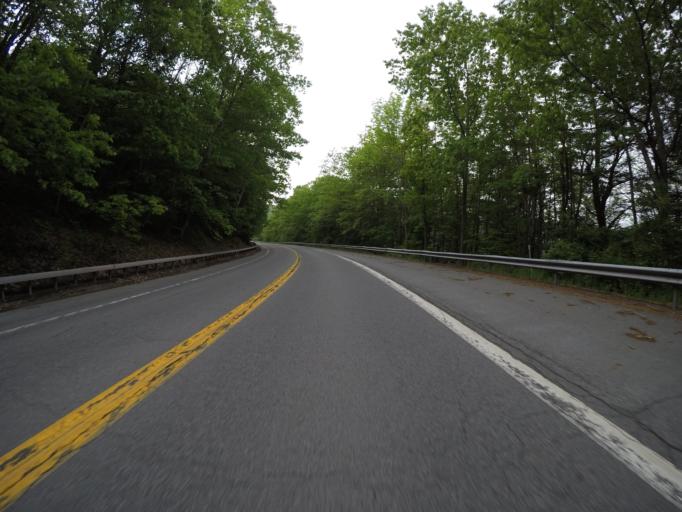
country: US
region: New York
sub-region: Sullivan County
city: Livingston Manor
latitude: 42.0895
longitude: -74.8359
